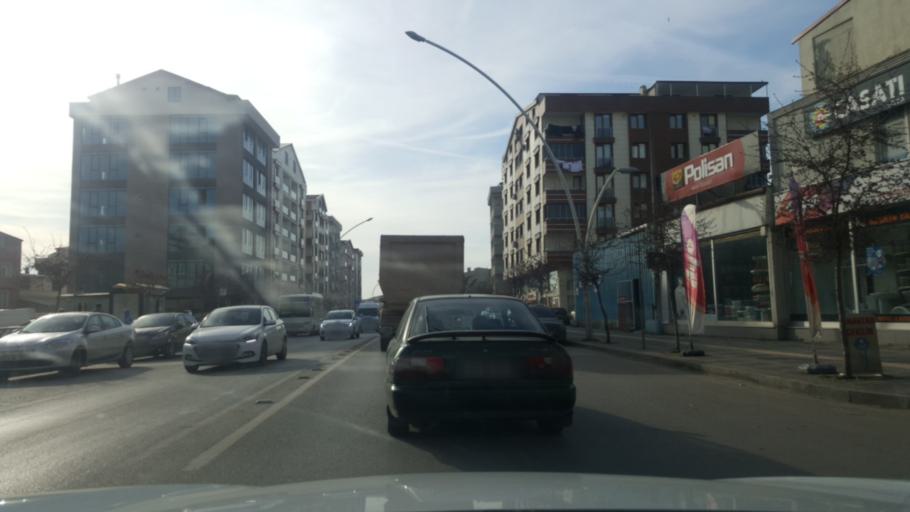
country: TR
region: Kocaeli
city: Gebze
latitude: 40.7919
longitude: 29.4357
